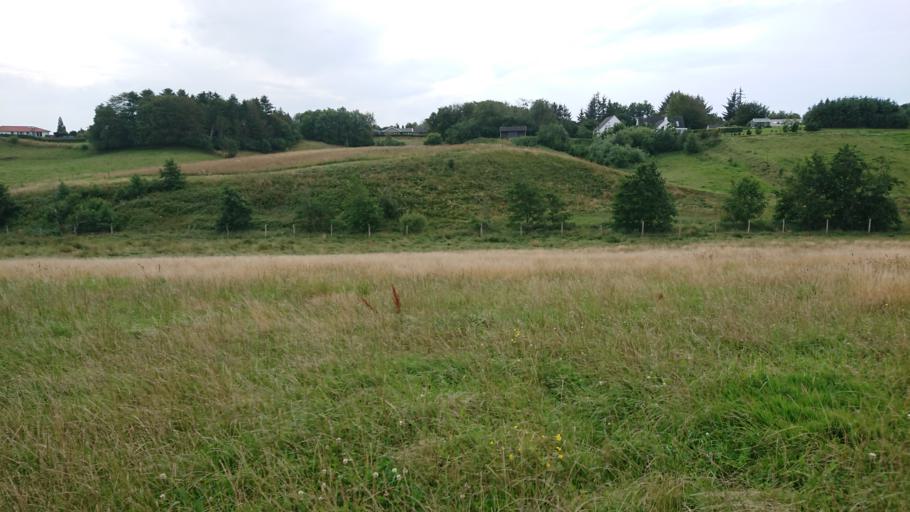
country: DK
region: North Denmark
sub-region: Hjorring Kommune
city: Sindal
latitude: 57.4754
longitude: 10.1782
